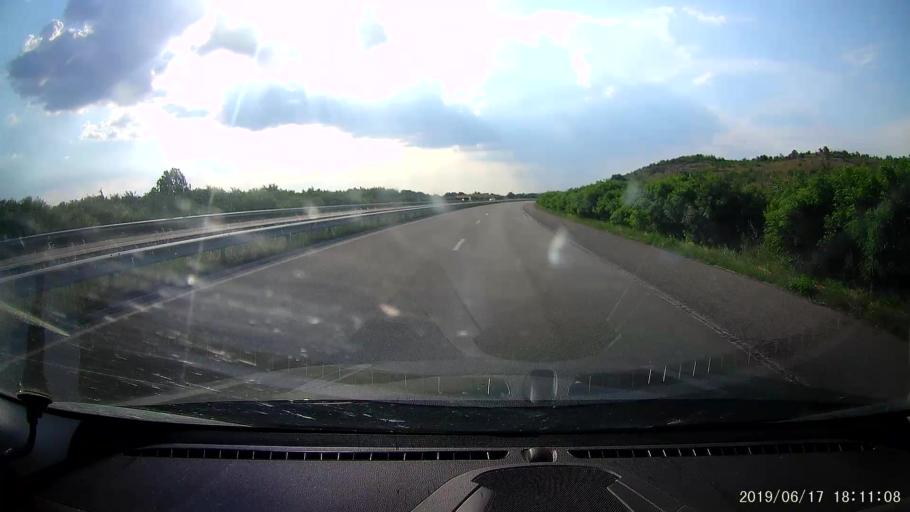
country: BG
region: Khaskovo
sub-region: Obshtina Lyubimets
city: Lyubimets
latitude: 41.8795
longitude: 26.0579
